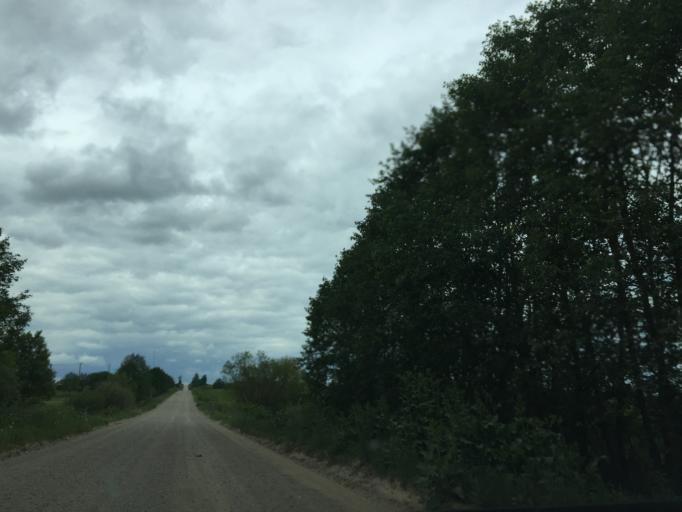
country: LV
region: Dagda
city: Dagda
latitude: 56.0053
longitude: 27.6053
